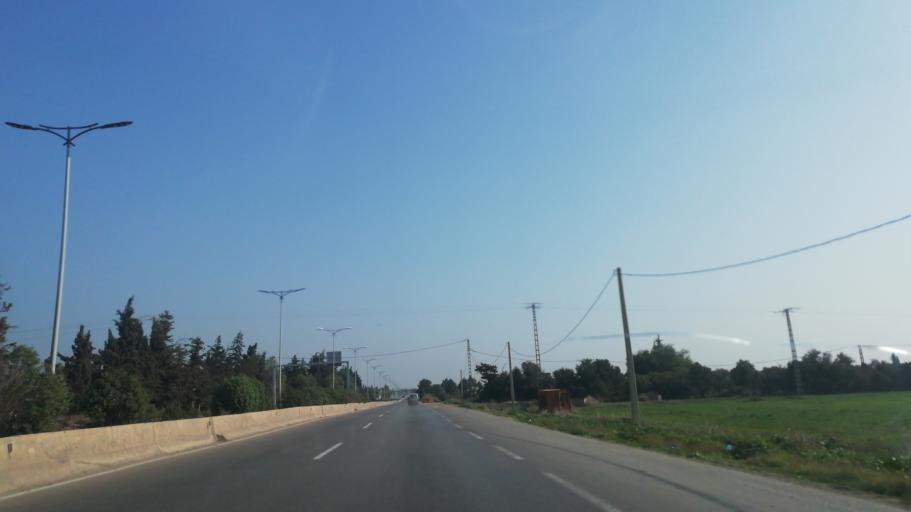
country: DZ
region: Oran
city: Bou Tlelis
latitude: 35.5728
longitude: -0.8747
